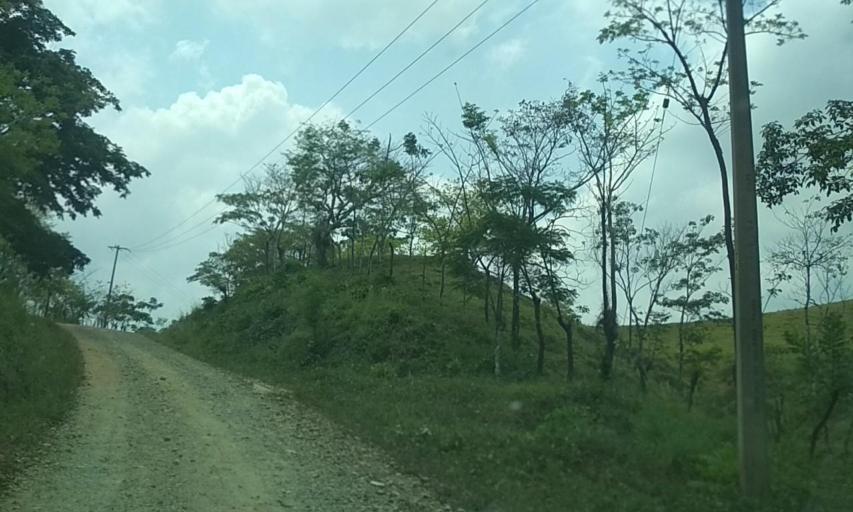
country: MX
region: Tabasco
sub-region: Huimanguillo
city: Francisco Rueda
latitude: 17.6048
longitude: -93.8049
